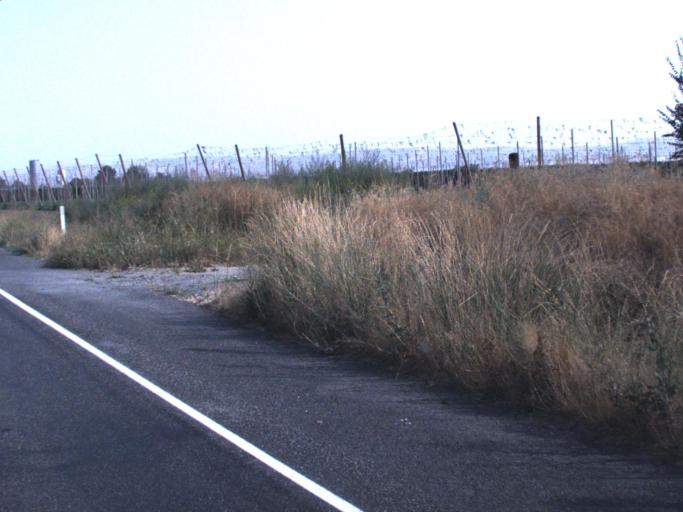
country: US
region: Washington
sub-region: Yakima County
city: Mabton
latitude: 46.2153
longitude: -120.0147
